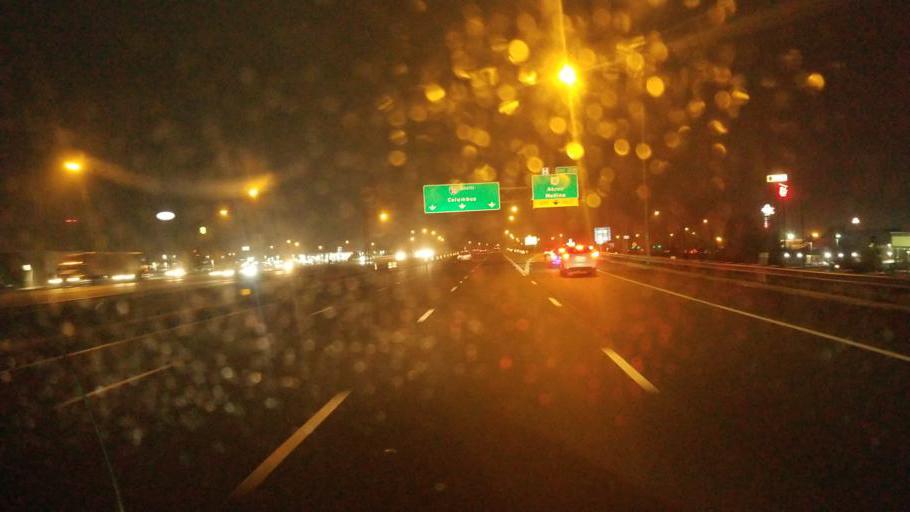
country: US
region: Ohio
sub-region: Medina County
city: Medina
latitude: 41.1399
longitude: -81.7931
